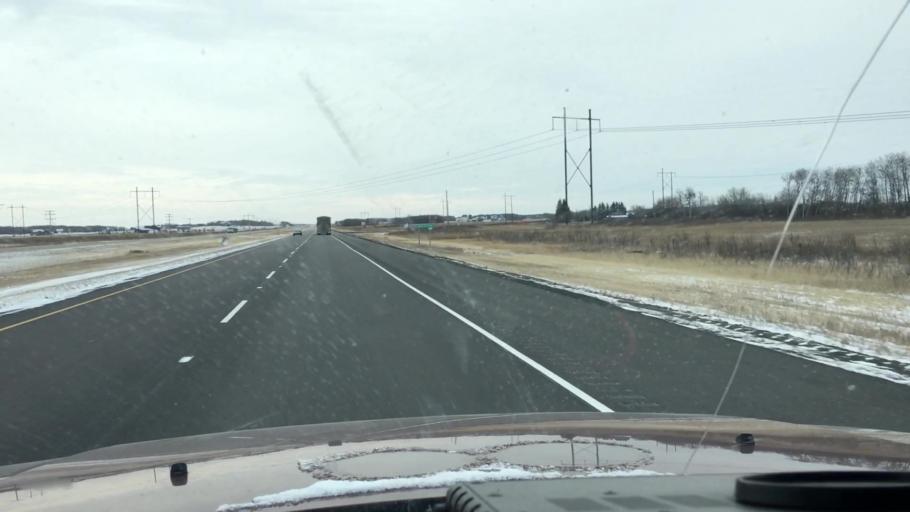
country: CA
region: Saskatchewan
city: Saskatoon
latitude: 51.9571
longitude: -106.5480
